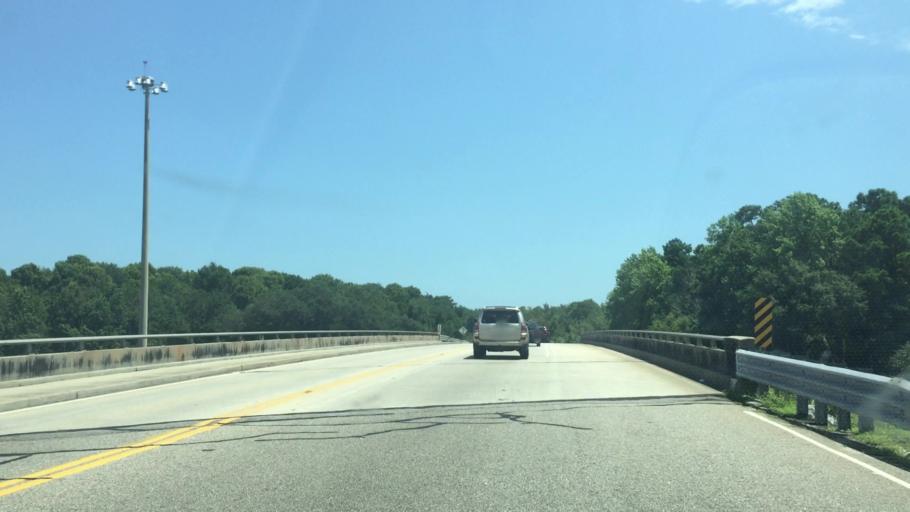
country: US
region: South Carolina
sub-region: Horry County
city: North Myrtle Beach
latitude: 33.8478
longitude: -78.6533
